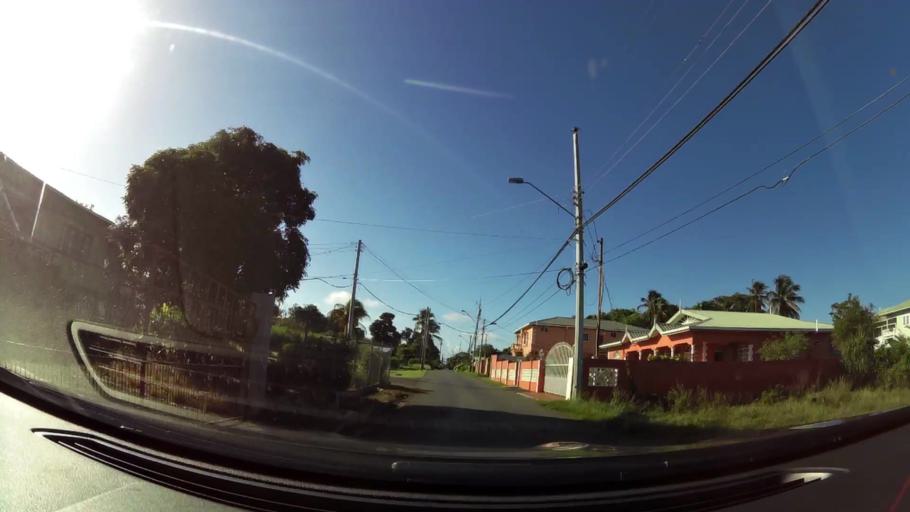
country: TT
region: Tobago
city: Scarborough
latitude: 11.1575
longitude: -60.8259
